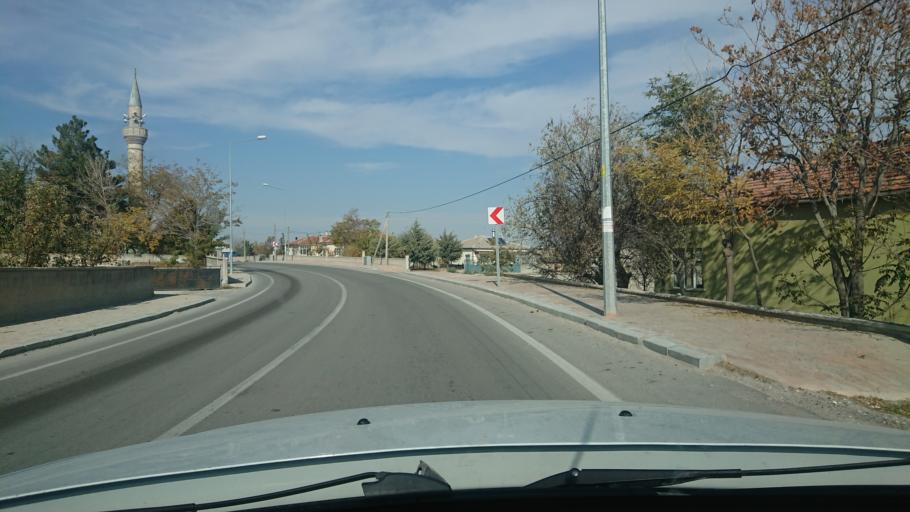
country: TR
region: Aksaray
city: Sultanhani
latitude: 38.2513
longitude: 33.4495
